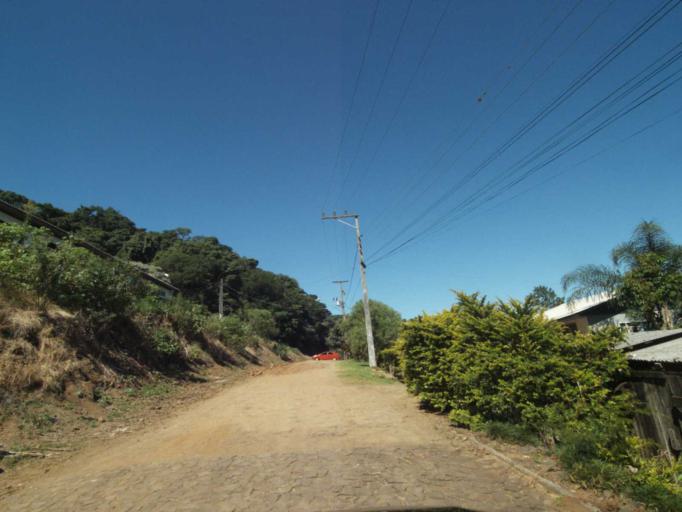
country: BR
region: Parana
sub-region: Francisco Beltrao
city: Francisco Beltrao
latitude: -26.1455
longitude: -53.3102
